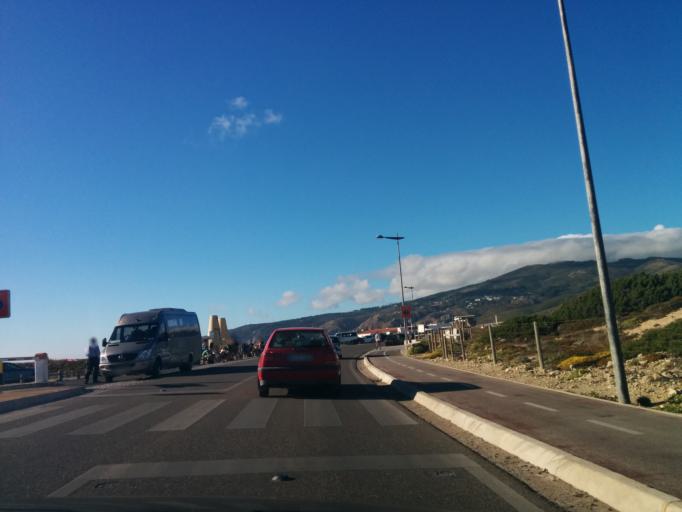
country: PT
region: Lisbon
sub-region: Cascais
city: Cascais
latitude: 38.7275
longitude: -9.4746
